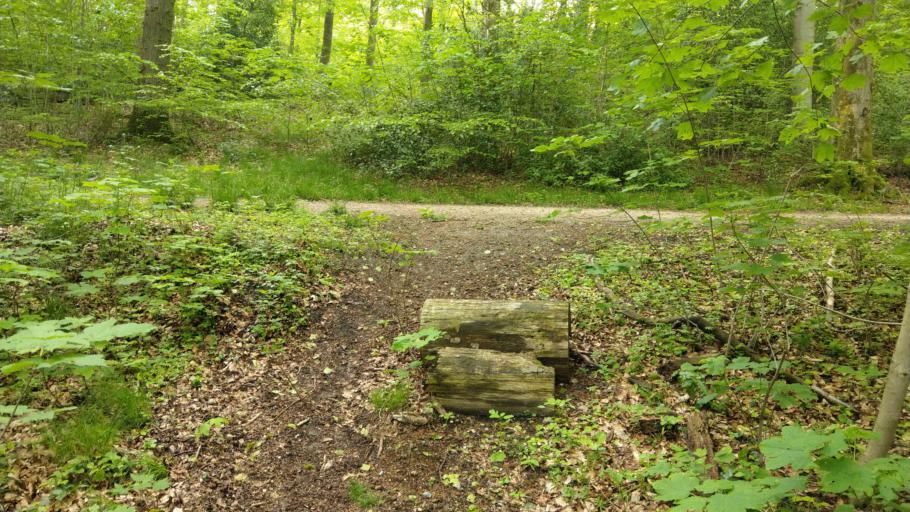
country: DE
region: North Rhine-Westphalia
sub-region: Regierungsbezirk Koln
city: Aachen
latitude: 50.7320
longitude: 6.0741
